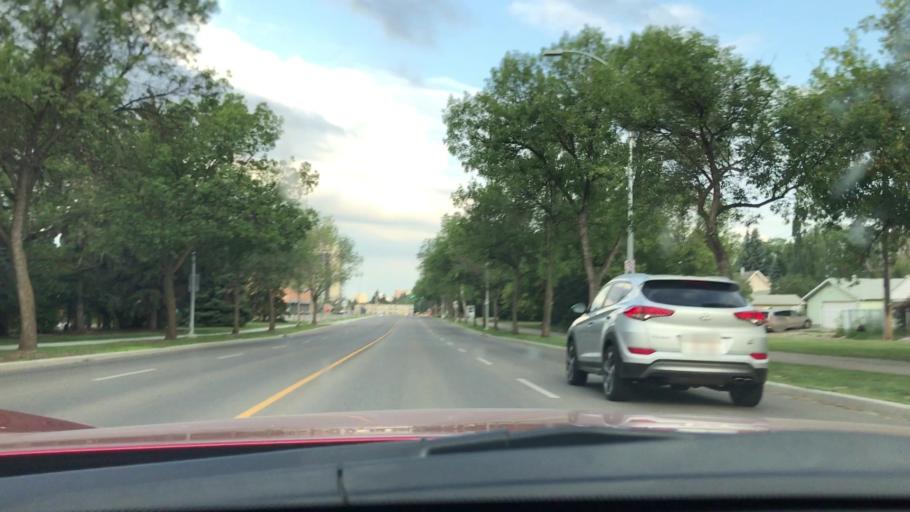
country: CA
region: Alberta
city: Edmonton
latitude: 53.5252
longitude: -113.4504
